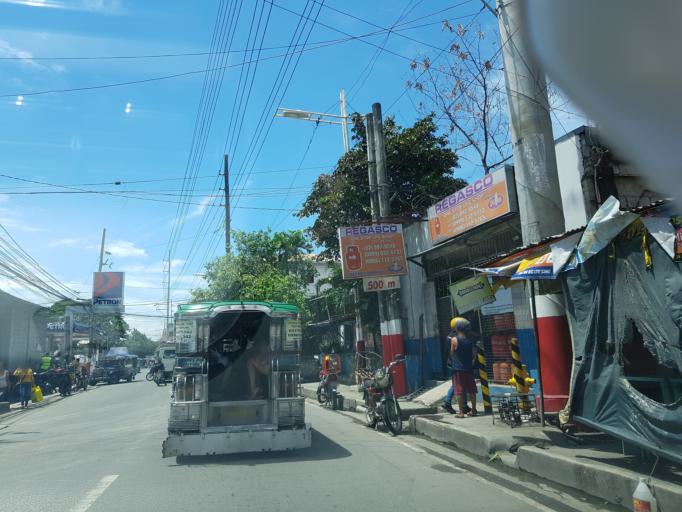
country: PH
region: Calabarzon
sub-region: Province of Rizal
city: Taguig
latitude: 14.4936
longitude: 121.0617
